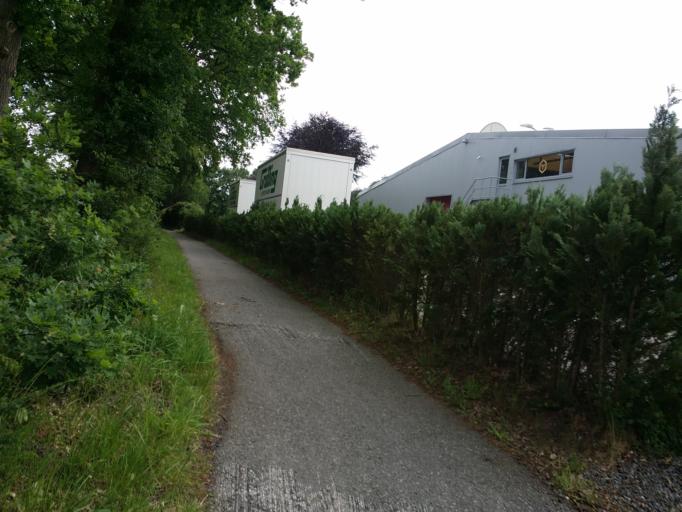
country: DE
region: Lower Saxony
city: Wiefelstede
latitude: 53.2925
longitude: 8.0699
